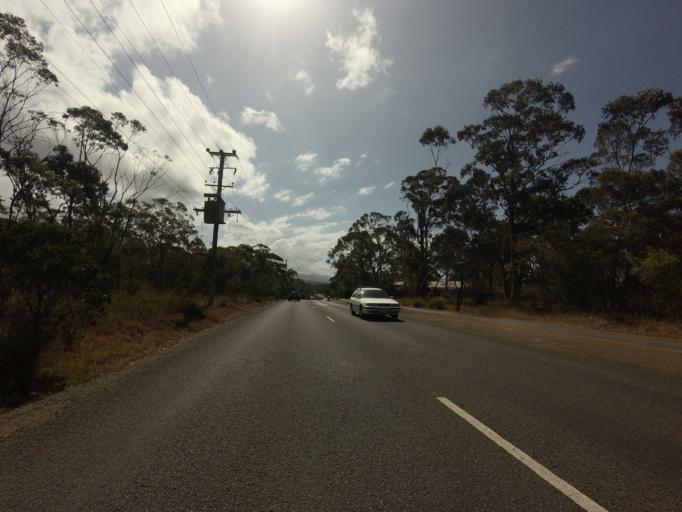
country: AU
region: Tasmania
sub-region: Hobart
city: Dynnyrne
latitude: -42.9175
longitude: 147.3186
